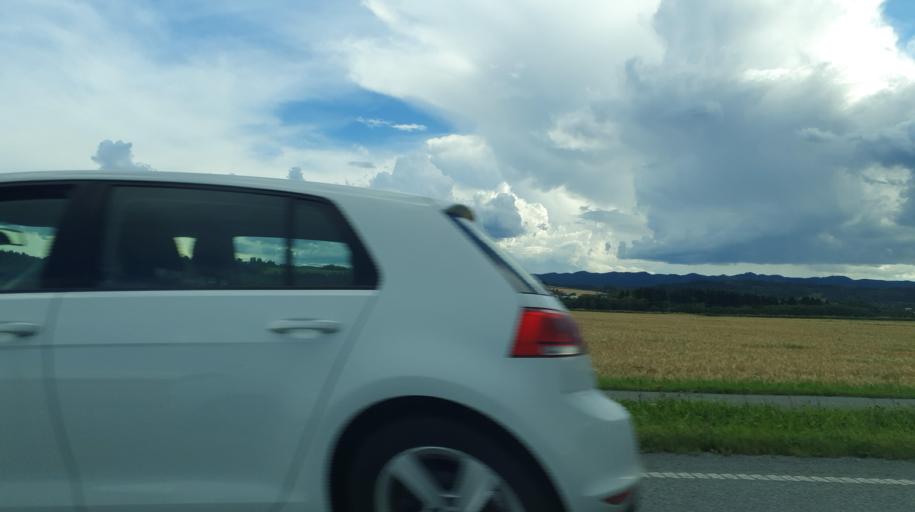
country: NO
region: Nord-Trondelag
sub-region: Levanger
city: Levanger
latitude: 63.7523
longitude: 11.3465
